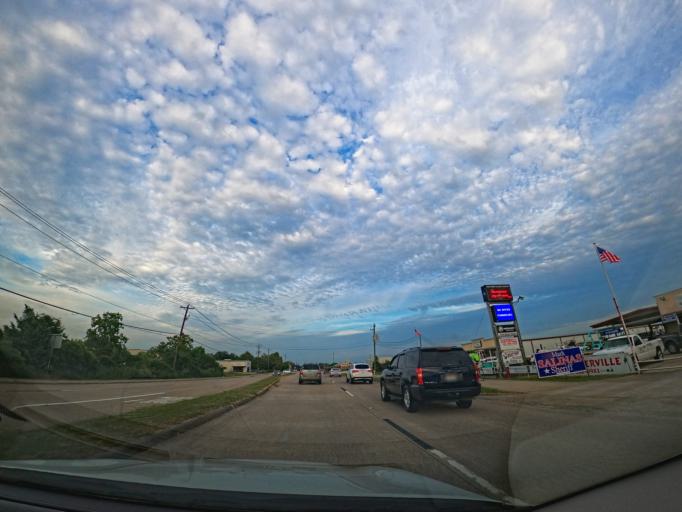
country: US
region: Texas
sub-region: Galveston County
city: Clear Lake Shores
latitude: 29.5300
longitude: -95.0324
